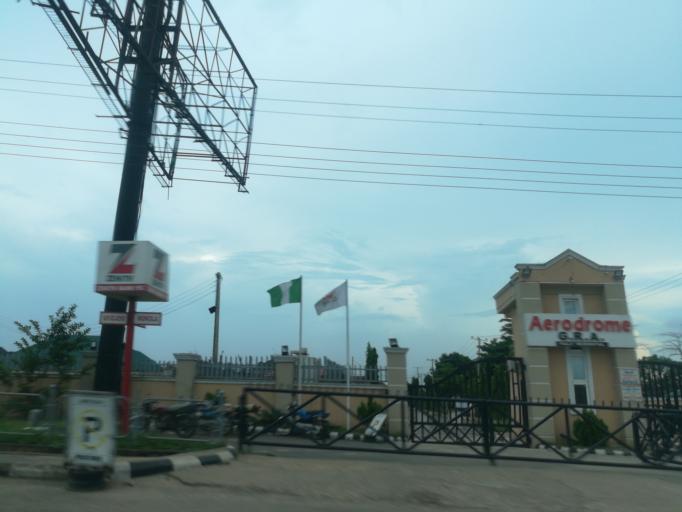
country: NG
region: Oyo
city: Ibadan
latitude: 7.4301
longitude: 3.9056
